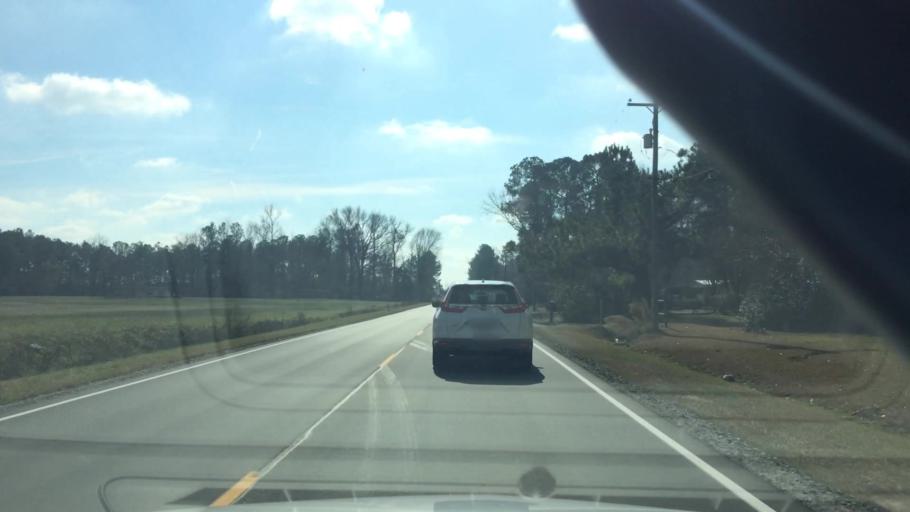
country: US
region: North Carolina
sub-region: Duplin County
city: Beulaville
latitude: 34.9360
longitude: -77.7706
